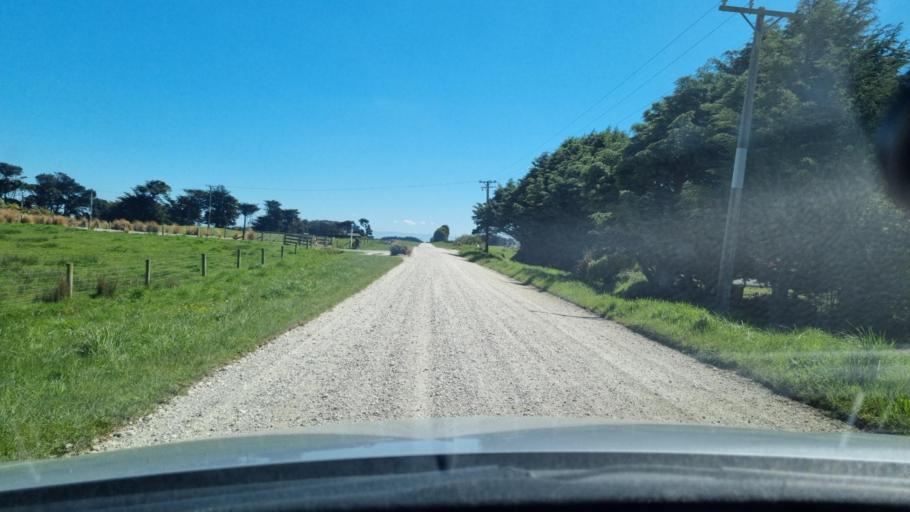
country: NZ
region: Southland
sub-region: Invercargill City
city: Invercargill
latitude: -46.4197
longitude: 168.2718
